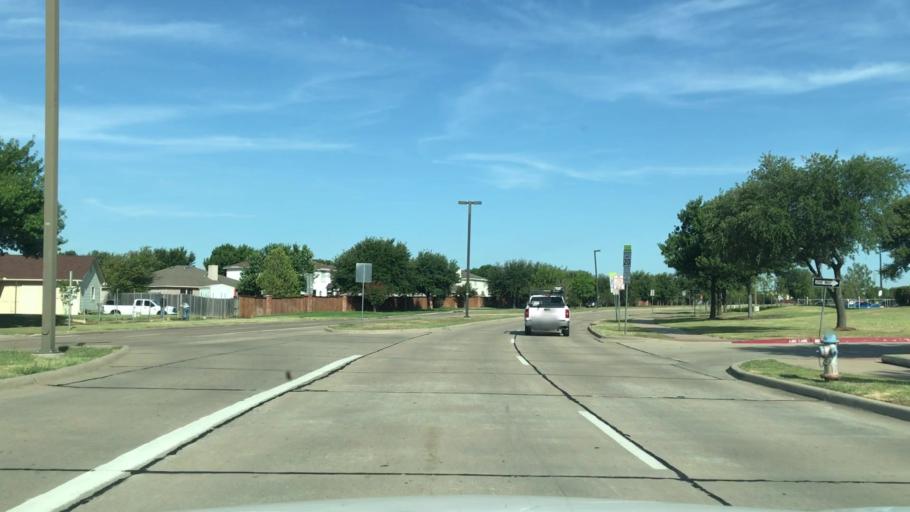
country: US
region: Texas
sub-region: Collin County
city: McKinney
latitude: 33.2295
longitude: -96.6419
